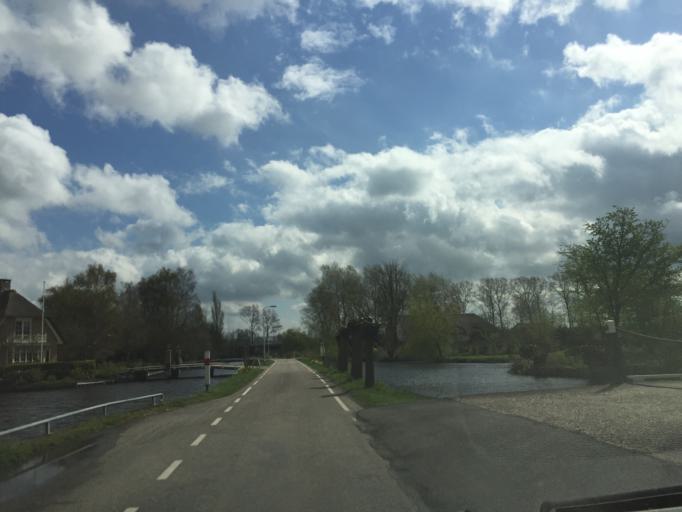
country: NL
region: South Holland
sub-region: Bodegraven-Reeuwijk
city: Reeuwijk
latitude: 52.0461
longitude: 4.7071
